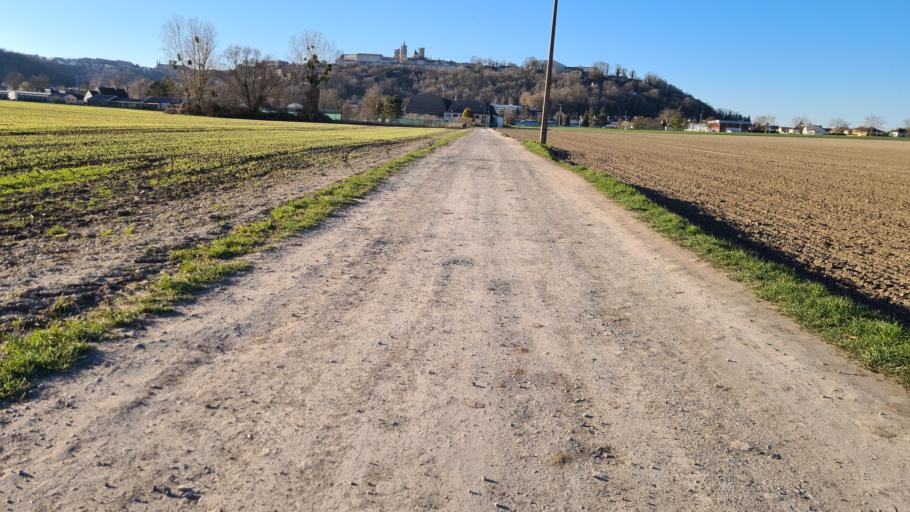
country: FR
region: Picardie
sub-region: Departement de l'Aisne
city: Laon
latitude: 49.5558
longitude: 3.6420
